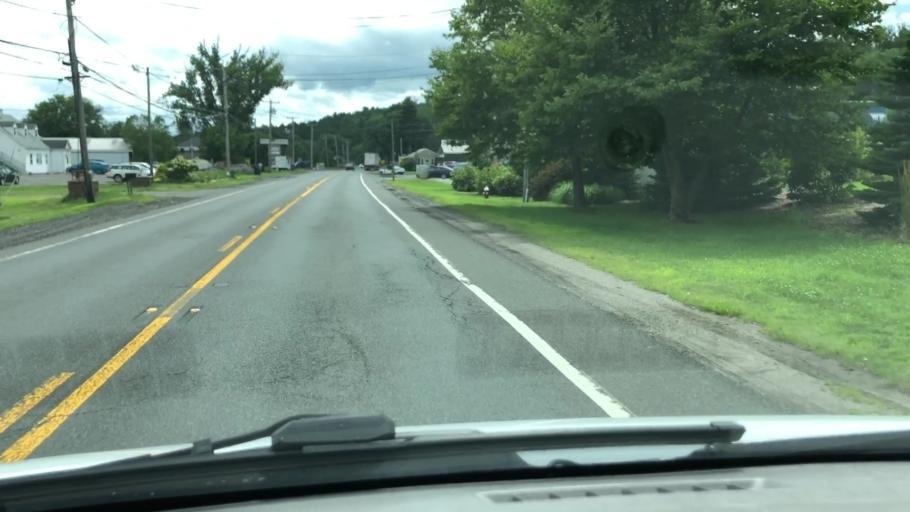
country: US
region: Massachusetts
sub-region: Hampshire County
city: Hatfield
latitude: 42.3691
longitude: -72.6366
